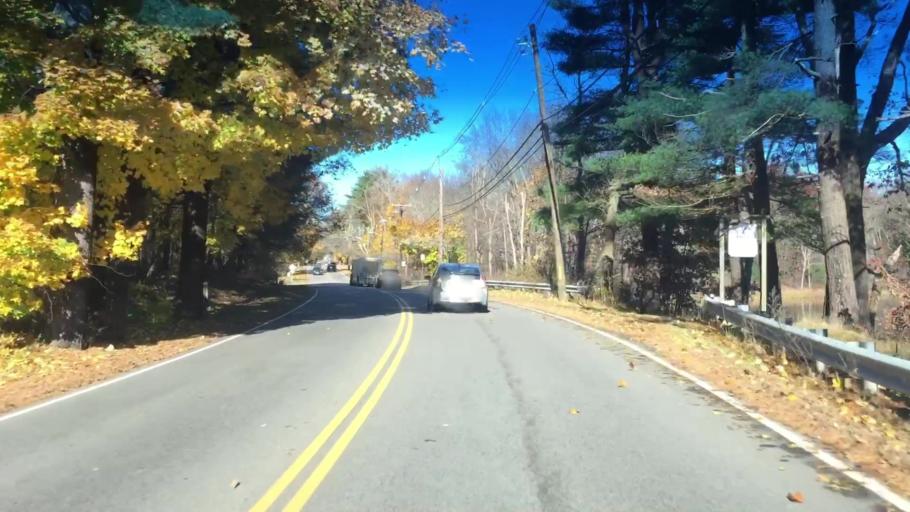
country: US
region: Massachusetts
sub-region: Norfolk County
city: Medfield
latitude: 42.1769
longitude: -71.3002
